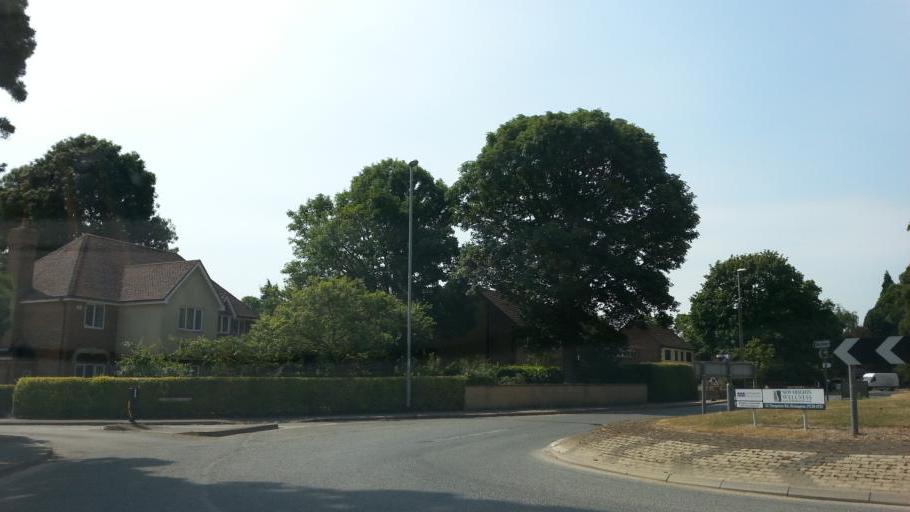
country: GB
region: England
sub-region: Cambridgeshire
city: Brampton
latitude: 52.3173
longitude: -0.2207
